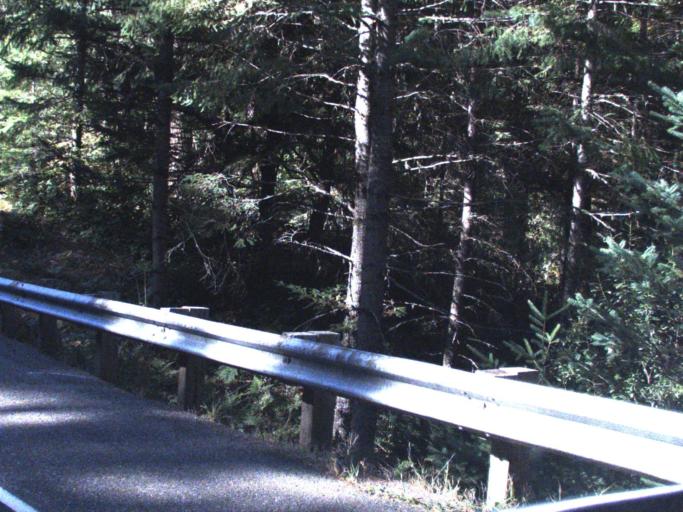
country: US
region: Washington
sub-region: Pierce County
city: Buckley
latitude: 46.6938
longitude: -121.5698
